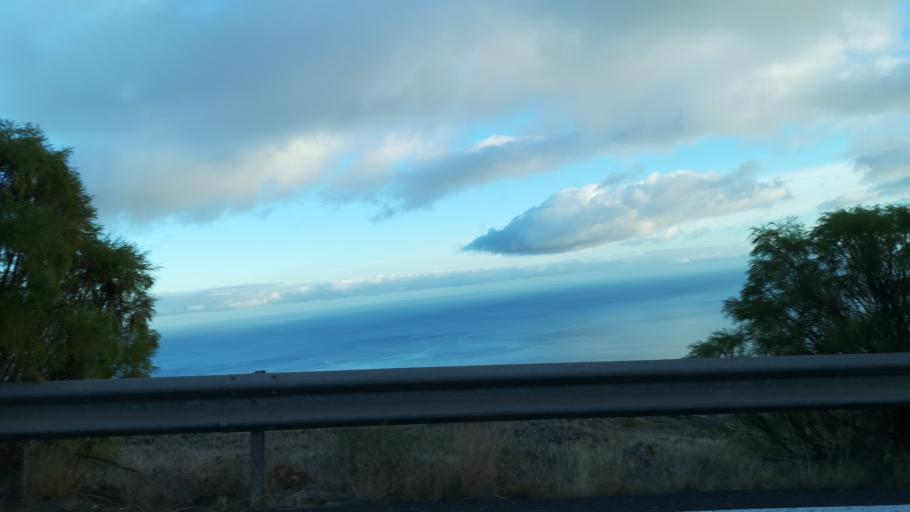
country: ES
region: Canary Islands
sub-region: Provincia de Santa Cruz de Tenerife
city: Alajero
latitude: 28.0423
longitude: -17.2313
